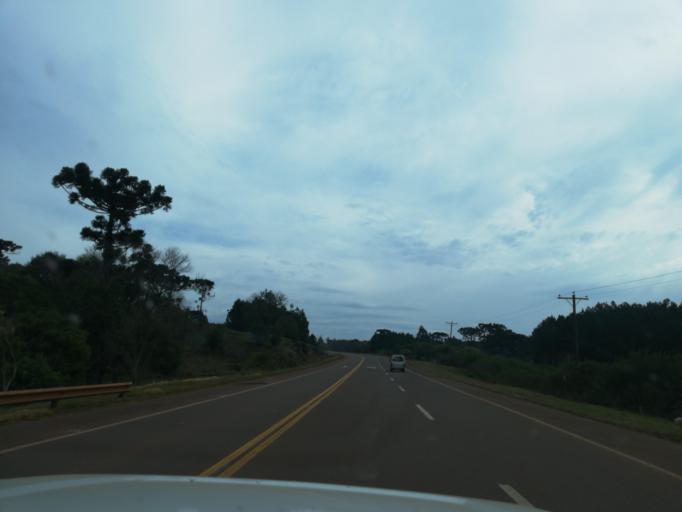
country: AR
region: Misiones
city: San Vicente
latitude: -26.6371
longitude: -54.1344
